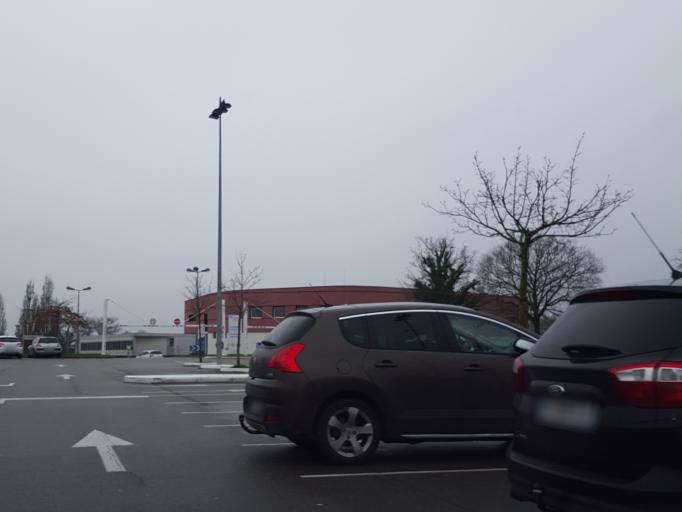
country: FR
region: Pays de la Loire
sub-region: Departement de la Vendee
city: La Roche-sur-Yon
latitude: 46.6711
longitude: -1.4064
